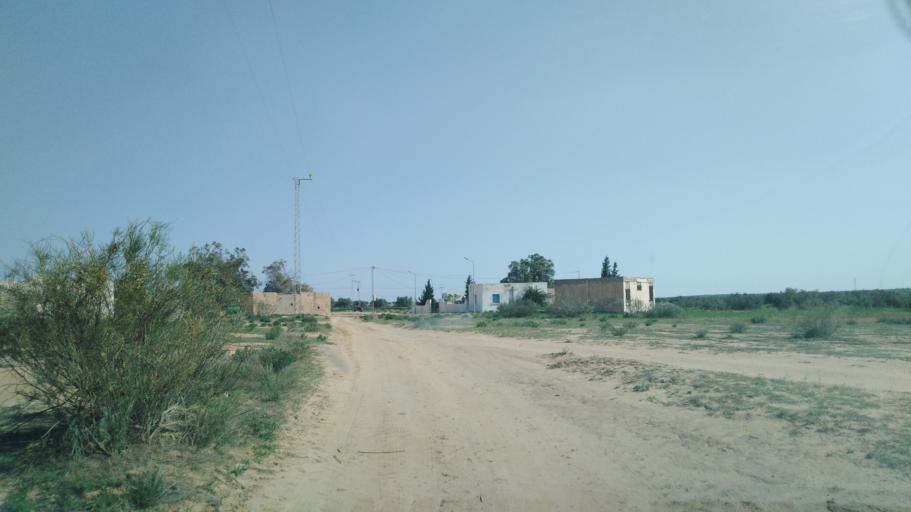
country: TN
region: Safaqis
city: Bi'r `Ali Bin Khalifah
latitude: 34.7785
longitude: 10.3655
